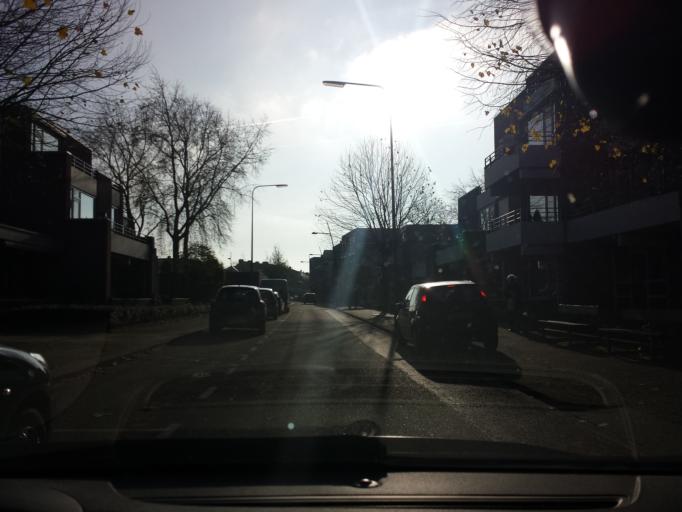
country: NL
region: Limburg
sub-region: Gemeente Heerlen
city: Heerlen
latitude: 50.8942
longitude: 6.0148
